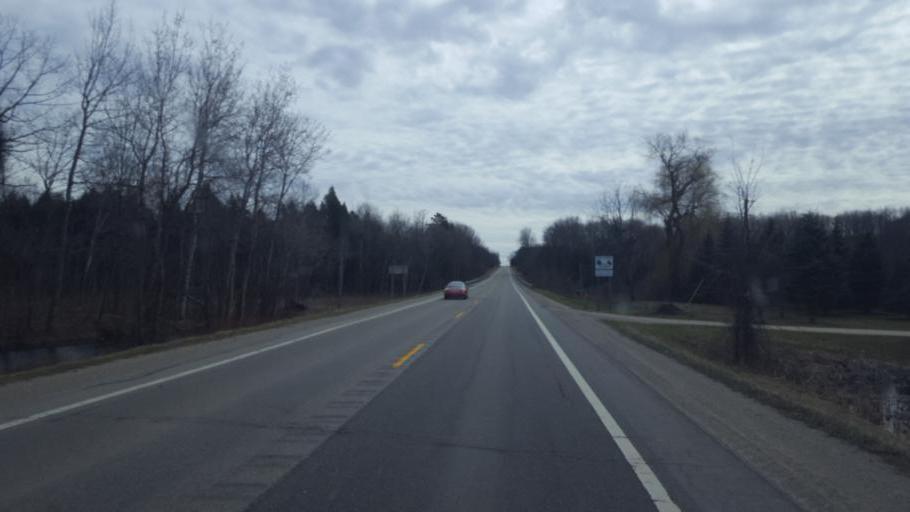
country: US
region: Michigan
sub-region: Isabella County
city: Lake Isabella
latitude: 43.6893
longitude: -85.1466
